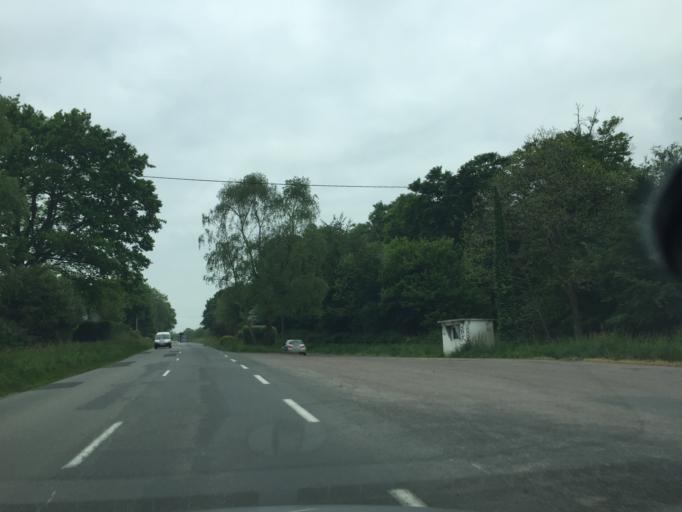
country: FR
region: Brittany
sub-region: Departement des Cotes-d'Armor
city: Henanbihen
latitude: 48.5560
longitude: -2.3820
